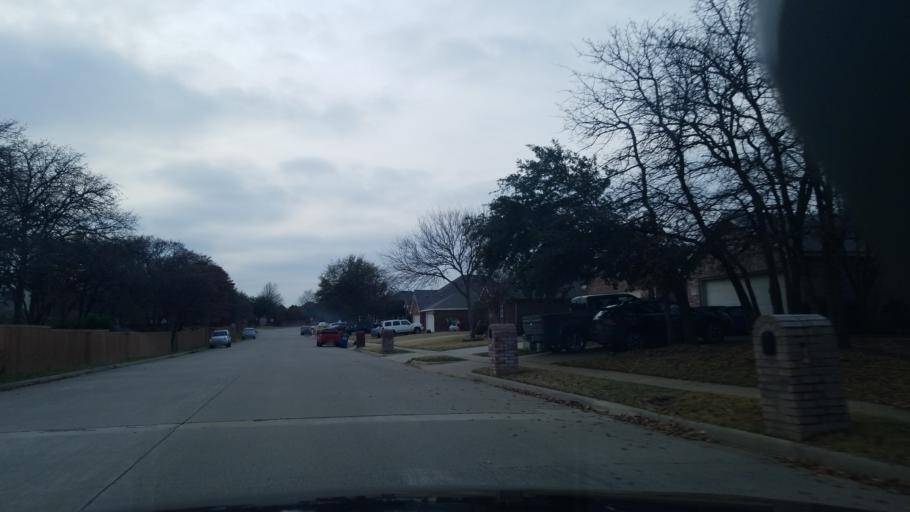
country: US
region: Texas
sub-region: Denton County
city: Corinth
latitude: 33.1359
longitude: -97.0824
